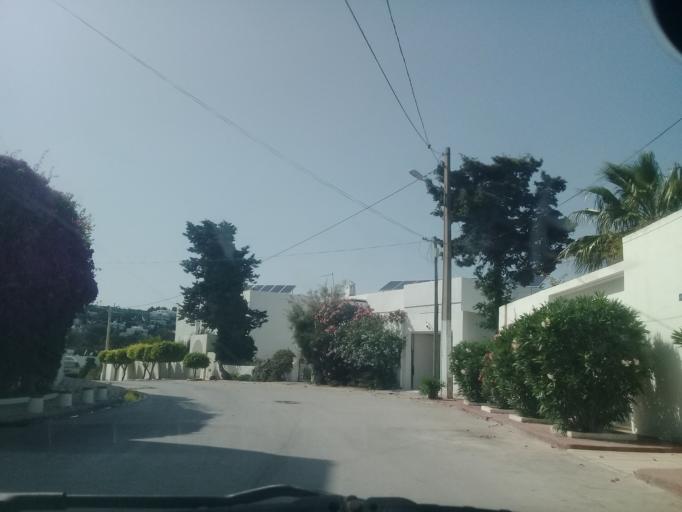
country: TN
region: Tunis
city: Al Marsa
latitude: 36.8901
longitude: 10.3246
